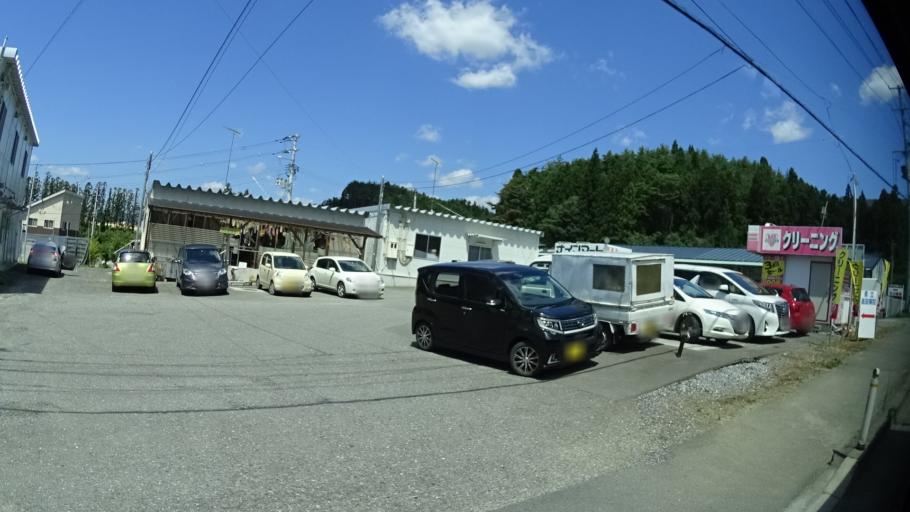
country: JP
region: Iwate
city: Ofunato
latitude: 39.0229
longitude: 141.6482
